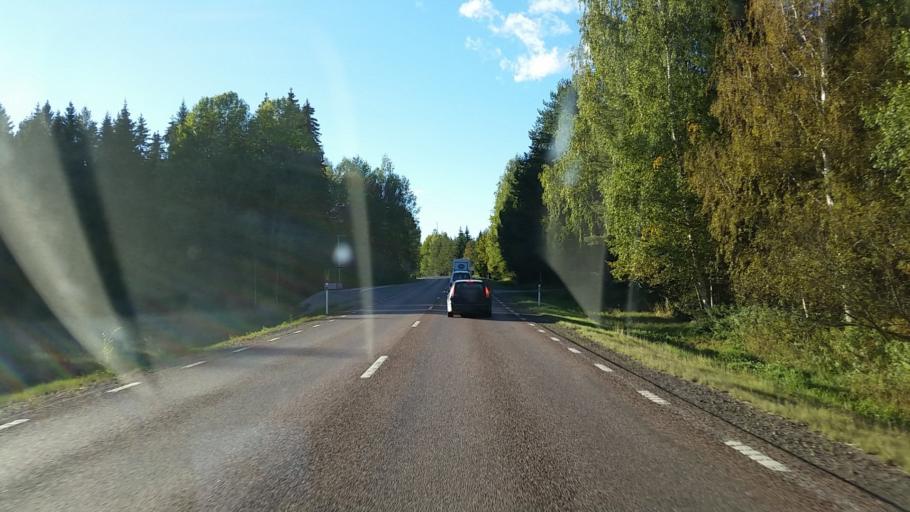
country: SE
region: Gaevleborg
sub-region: Hudiksvalls Kommun
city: Delsbo
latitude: 61.8032
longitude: 16.4704
